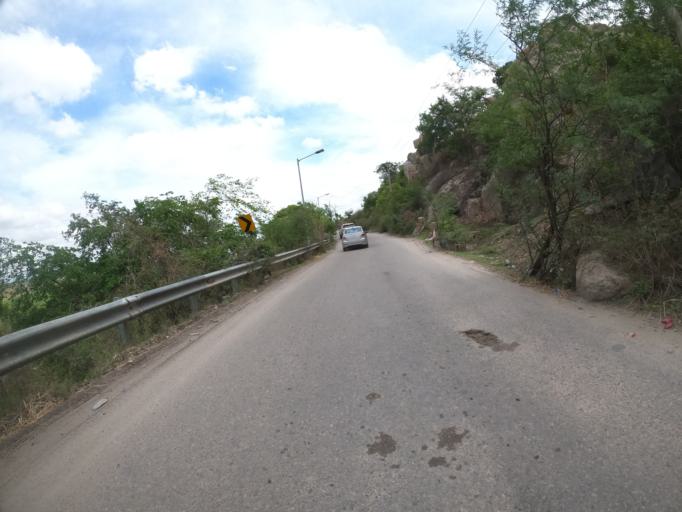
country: IN
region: Telangana
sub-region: Hyderabad
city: Hyderabad
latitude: 17.3176
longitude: 78.3710
